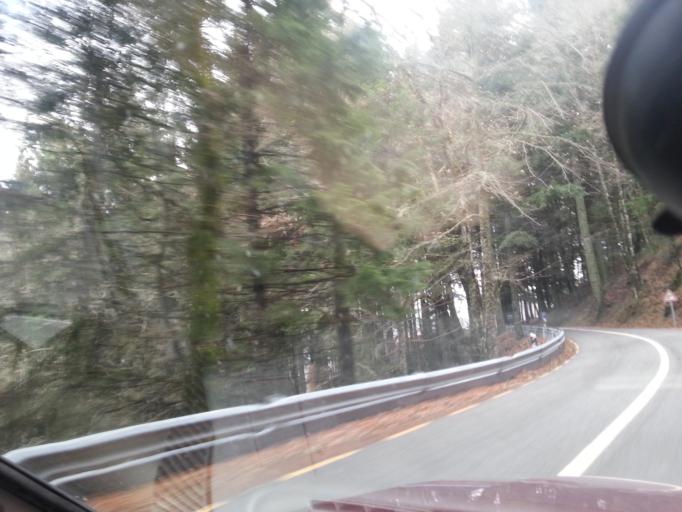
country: PT
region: Guarda
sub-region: Manteigas
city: Manteigas
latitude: 40.4112
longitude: -7.5534
